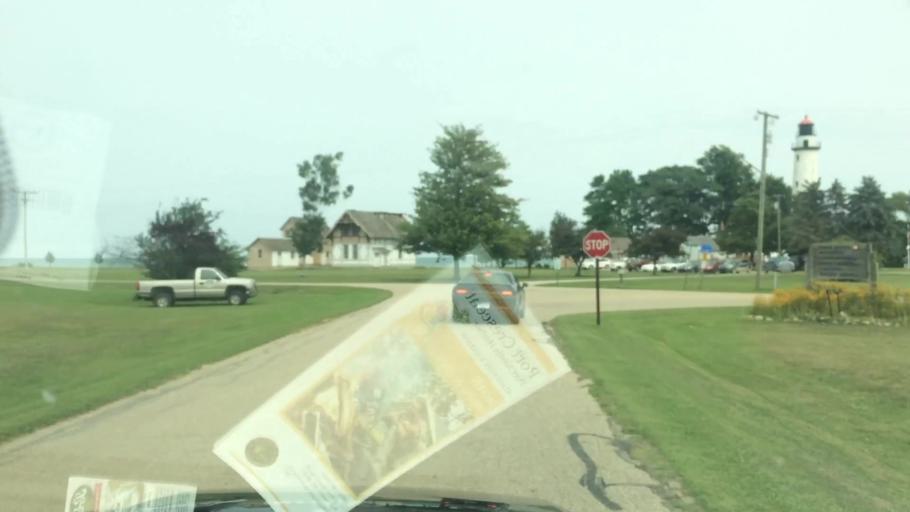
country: US
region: Michigan
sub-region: Huron County
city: Harbor Beach
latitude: 44.0216
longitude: -82.7945
